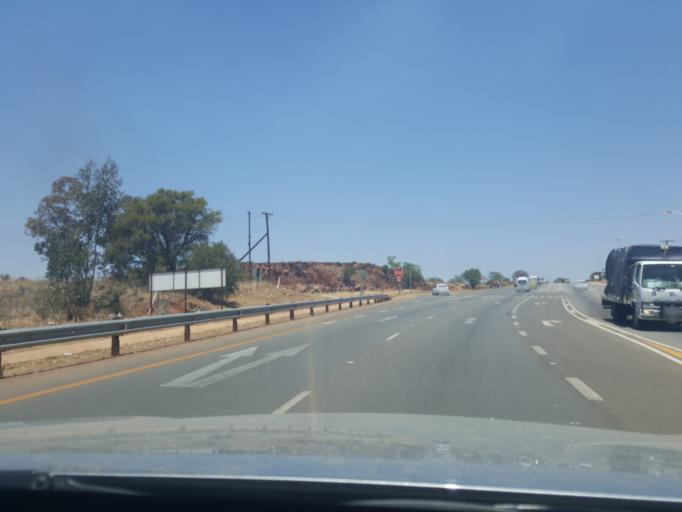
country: ZA
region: North-West
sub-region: Ngaka Modiri Molema District Municipality
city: Zeerust
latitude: -25.5493
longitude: 26.0732
